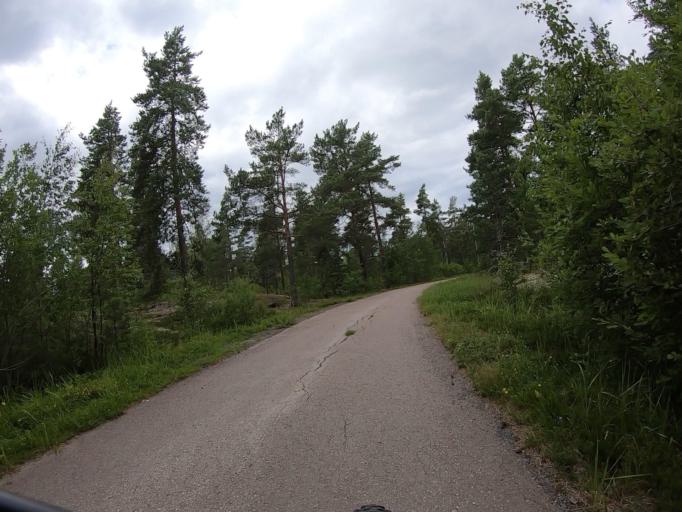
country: FI
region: Varsinais-Suomi
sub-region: Vakka-Suomi
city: Uusikaupunki
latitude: 60.8175
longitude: 21.4152
